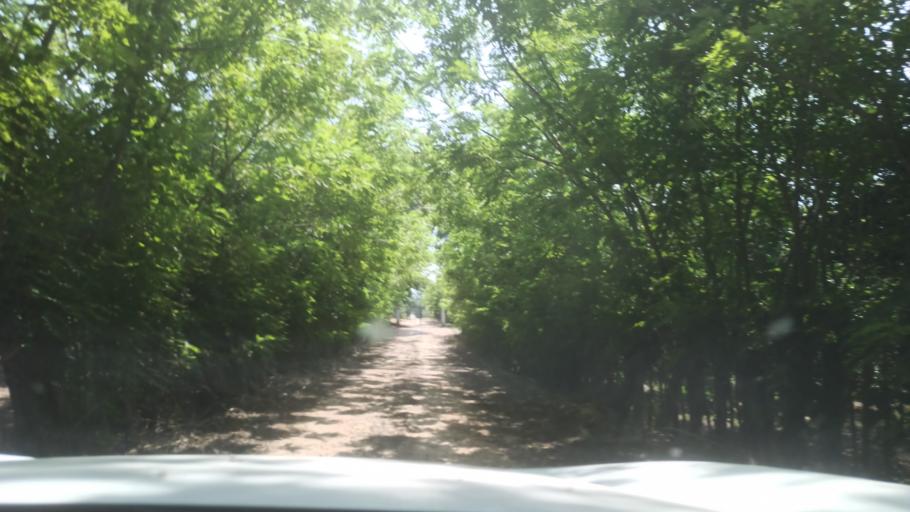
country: MX
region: Veracruz
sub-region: Atzalan
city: Colonias Pedernales
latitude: 20.0376
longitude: -97.0051
